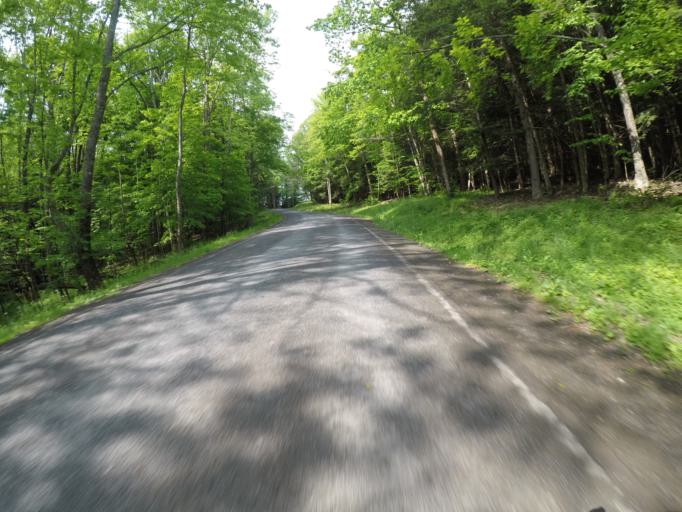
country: US
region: New York
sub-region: Delaware County
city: Stamford
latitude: 42.1519
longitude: -74.6675
